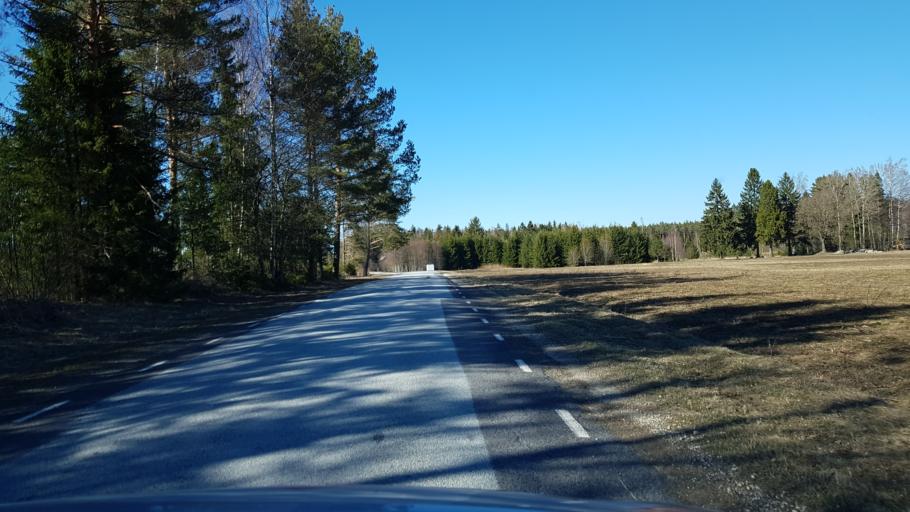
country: EE
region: Laeaene-Virumaa
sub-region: Viru-Nigula vald
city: Kunda
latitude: 59.3766
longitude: 26.5781
